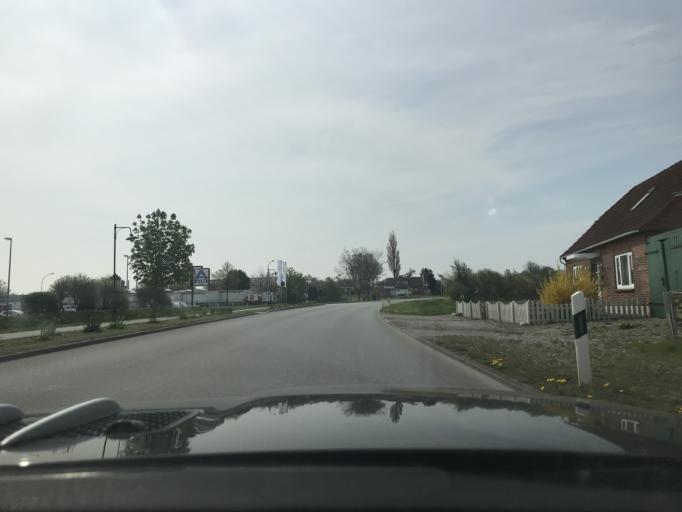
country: DE
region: Schleswig-Holstein
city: Grube
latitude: 54.2244
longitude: 11.0345
